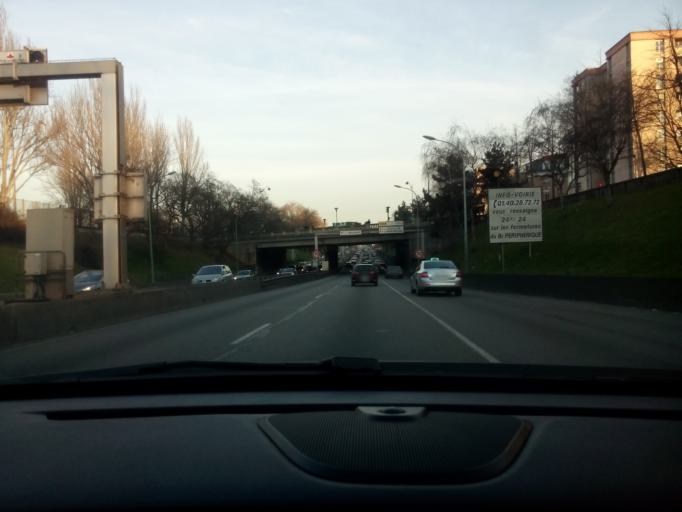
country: FR
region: Ile-de-France
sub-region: Departement des Hauts-de-Seine
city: Malakoff
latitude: 48.8256
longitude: 2.3005
